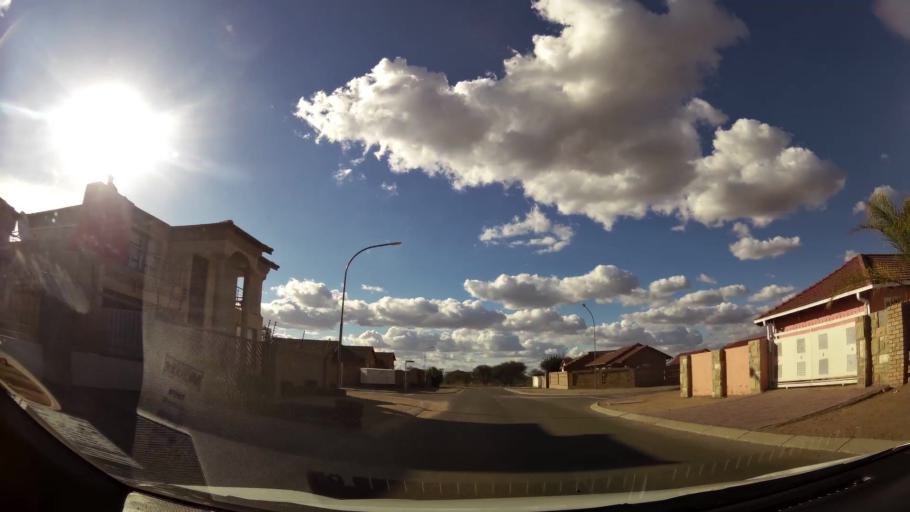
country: ZA
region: Limpopo
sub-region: Capricorn District Municipality
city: Polokwane
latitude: -23.9383
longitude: 29.4431
